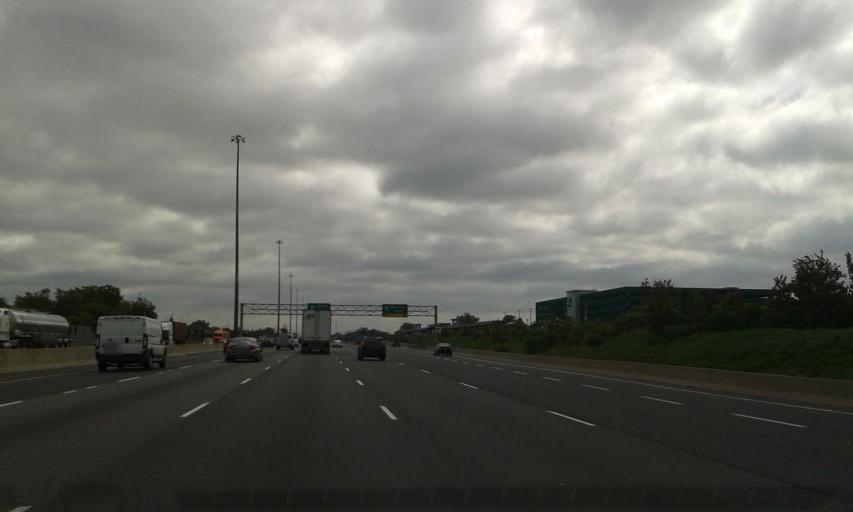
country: CA
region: Ontario
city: Ajax
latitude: 43.8477
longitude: -79.0471
